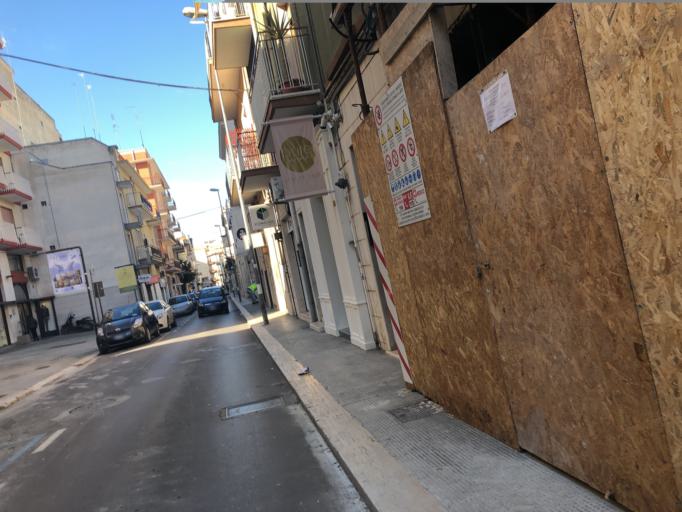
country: IT
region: Apulia
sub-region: Provincia di Barletta - Andria - Trani
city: Andria
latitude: 41.2283
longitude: 16.3020
